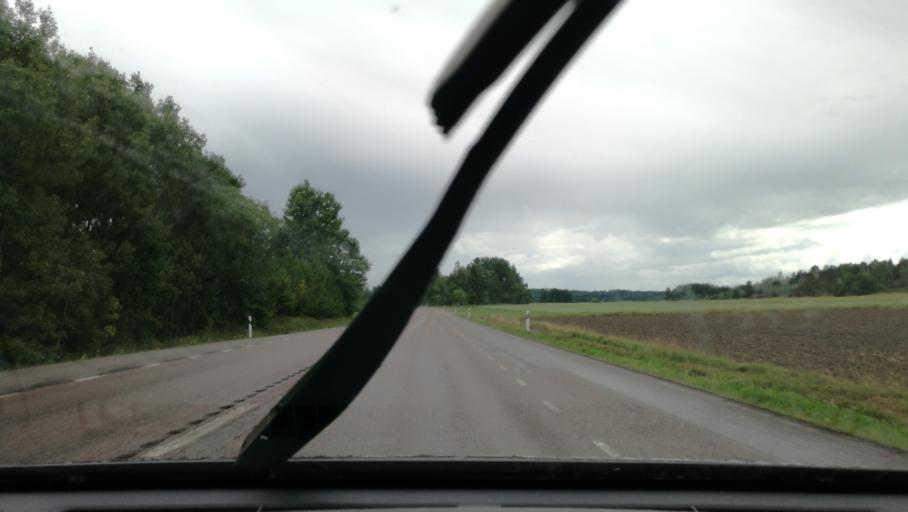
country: SE
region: Vaestmanland
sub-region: Kungsors Kommun
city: Kungsoer
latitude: 59.4455
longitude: 16.0441
